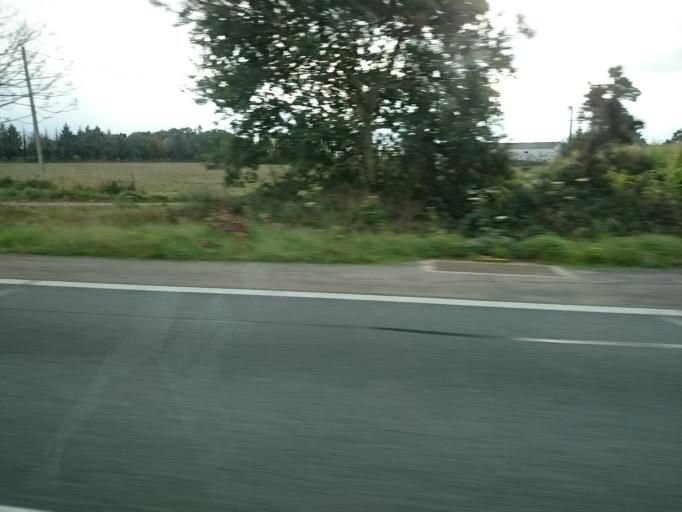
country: FR
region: Brittany
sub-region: Departement des Cotes-d'Armor
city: Plestan
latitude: 48.4124
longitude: -2.4281
